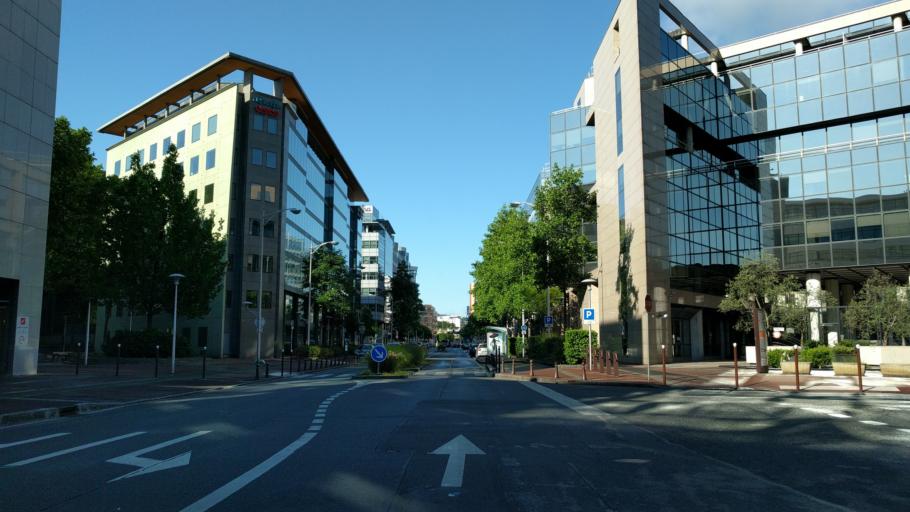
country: FR
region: Ile-de-France
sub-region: Departement des Hauts-de-Seine
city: Issy-les-Moulineaux
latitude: 48.8312
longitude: 2.2667
